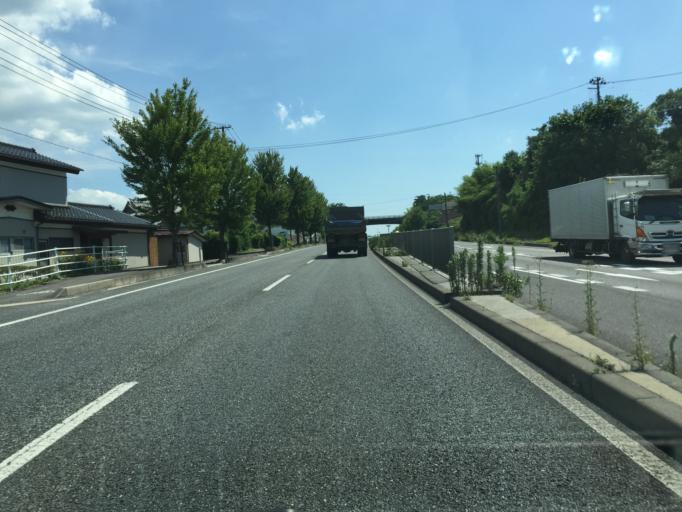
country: JP
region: Fukushima
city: Motomiya
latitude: 37.5091
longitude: 140.3952
